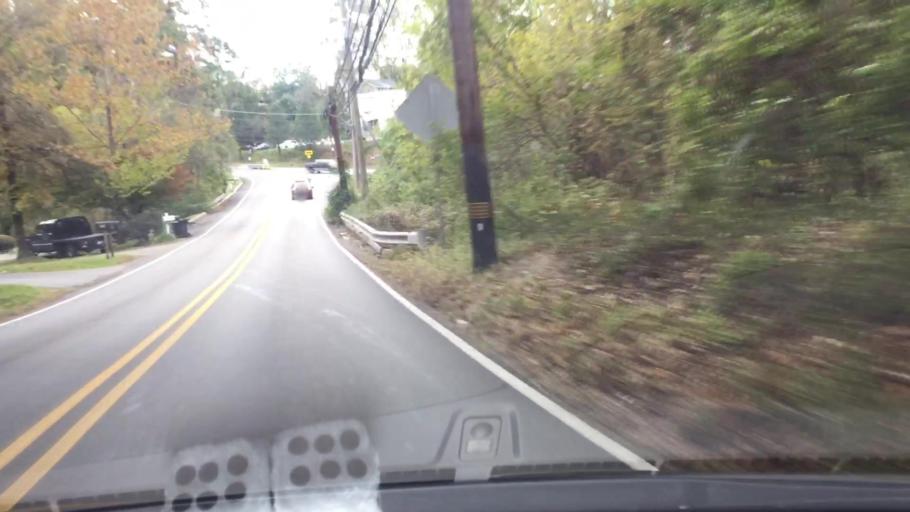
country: US
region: Pennsylvania
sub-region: Delaware County
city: Media
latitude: 39.9179
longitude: -75.4025
